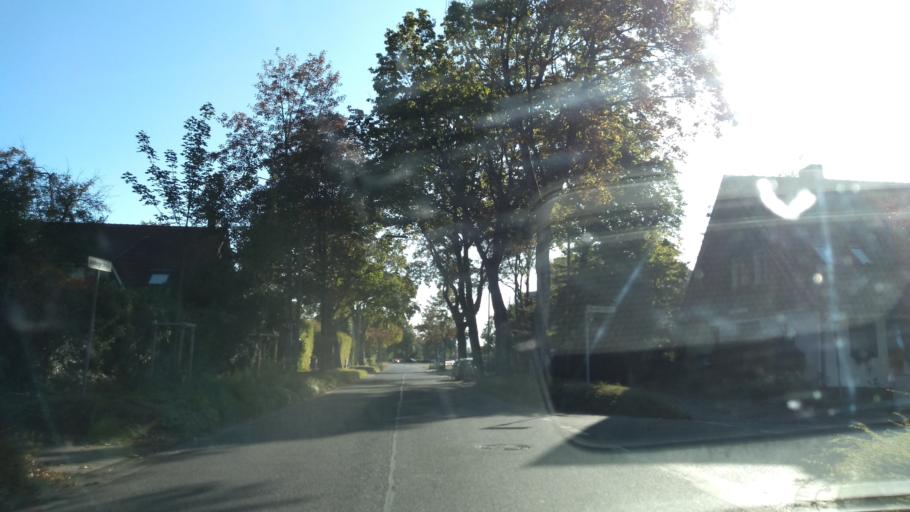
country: DE
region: North Rhine-Westphalia
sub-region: Regierungsbezirk Dusseldorf
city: Dinslaken
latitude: 51.5541
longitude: 6.7308
